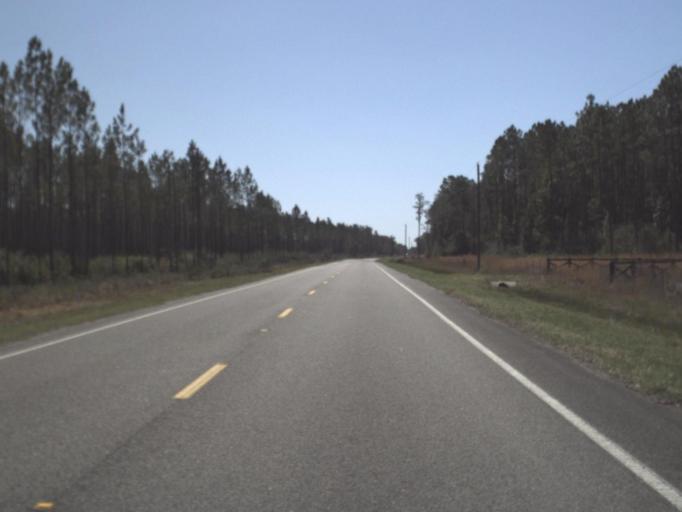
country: US
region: Florida
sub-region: Leon County
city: Woodville
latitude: 30.2713
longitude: -84.0422
